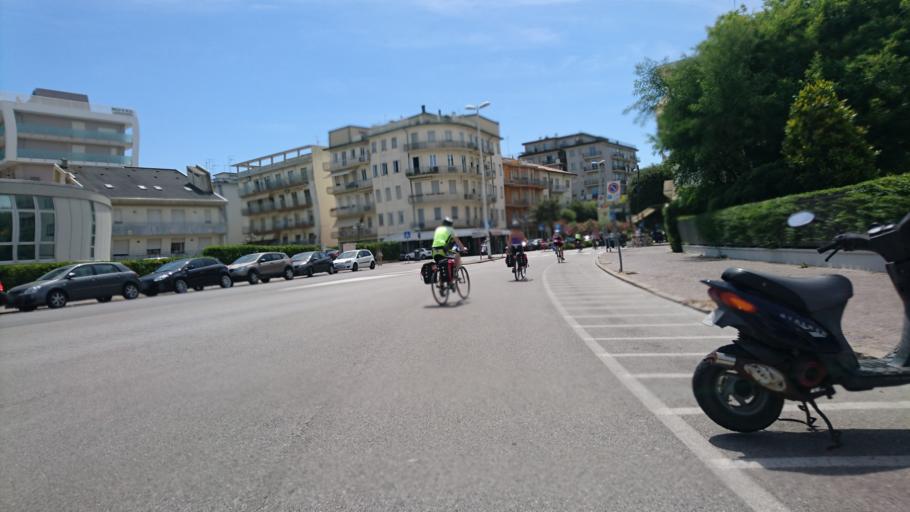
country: IT
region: Veneto
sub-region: Provincia di Venezia
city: Chioggia
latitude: 45.2124
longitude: 12.2946
